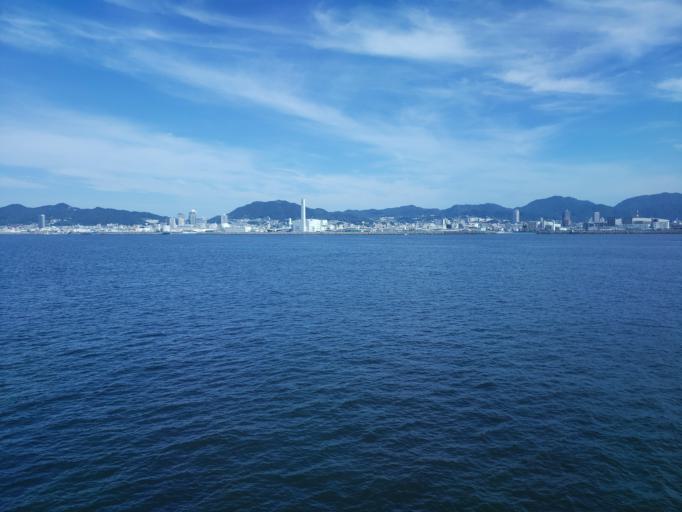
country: JP
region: Hyogo
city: Kobe
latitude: 34.6368
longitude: 135.1709
